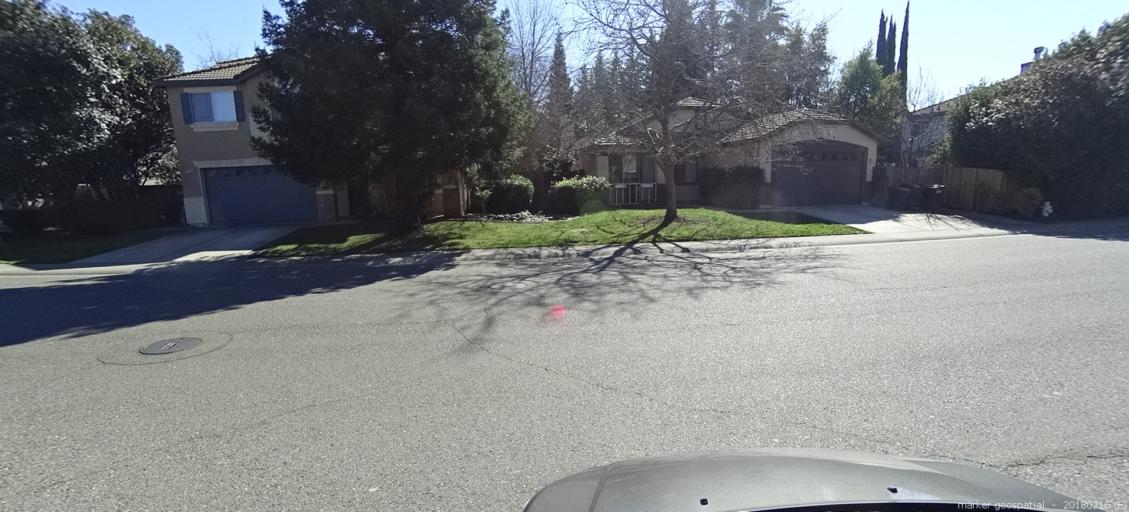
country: US
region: California
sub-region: Sacramento County
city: Gold River
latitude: 38.6190
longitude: -121.2583
